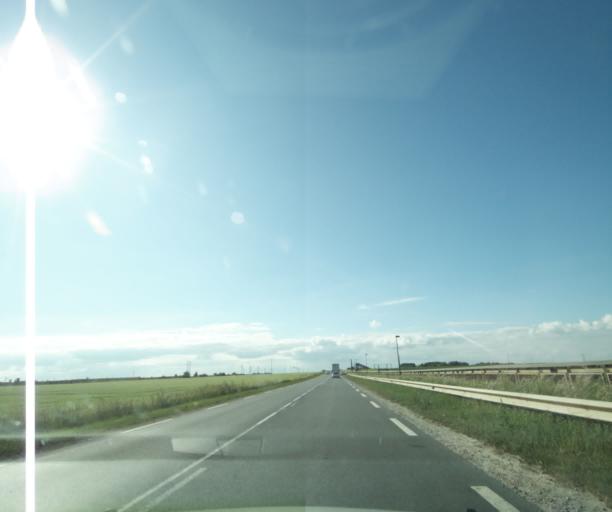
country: FR
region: Centre
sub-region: Departement d'Eure-et-Loir
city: Voves
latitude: 48.2894
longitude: 1.7164
